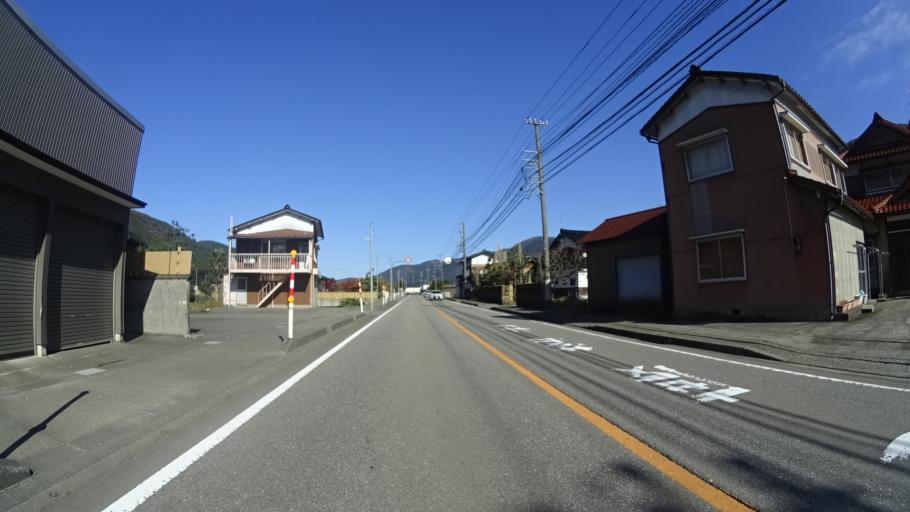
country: JP
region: Ishikawa
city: Tsurugi-asahimachi
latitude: 36.4131
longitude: 136.6320
